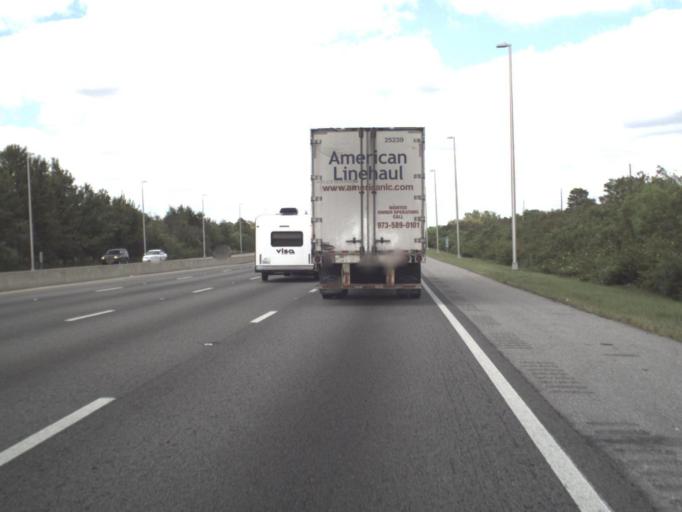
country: US
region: Florida
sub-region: Orange County
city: Oak Ridge
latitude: 28.4579
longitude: -81.4283
